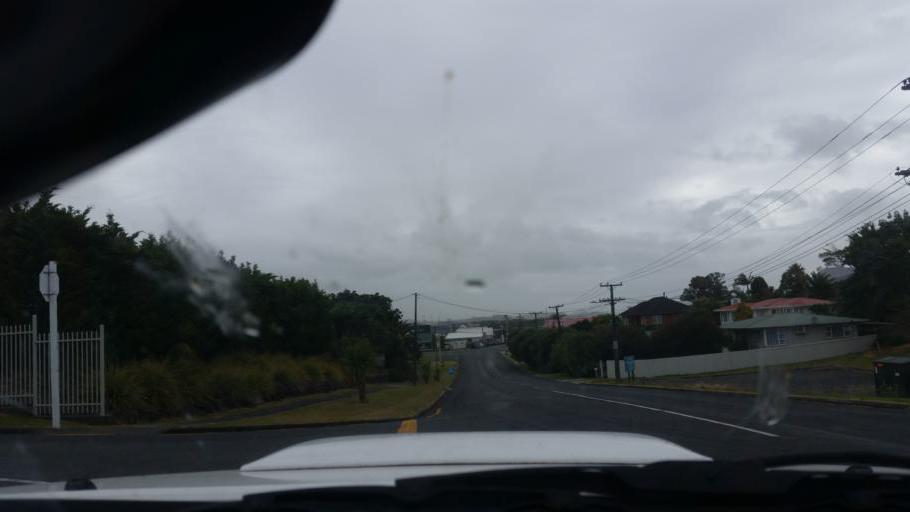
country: NZ
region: Northland
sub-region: Kaipara District
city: Dargaville
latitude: -35.9381
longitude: 173.8686
